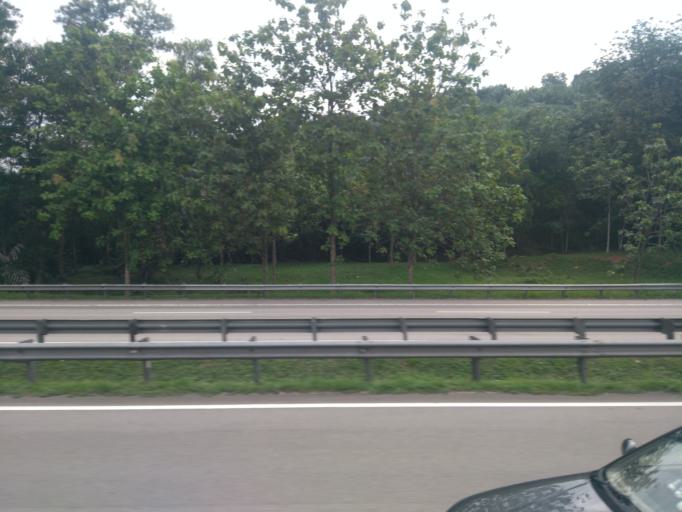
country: MY
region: Negeri Sembilan
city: Seremban
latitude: 2.6537
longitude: 101.9904
